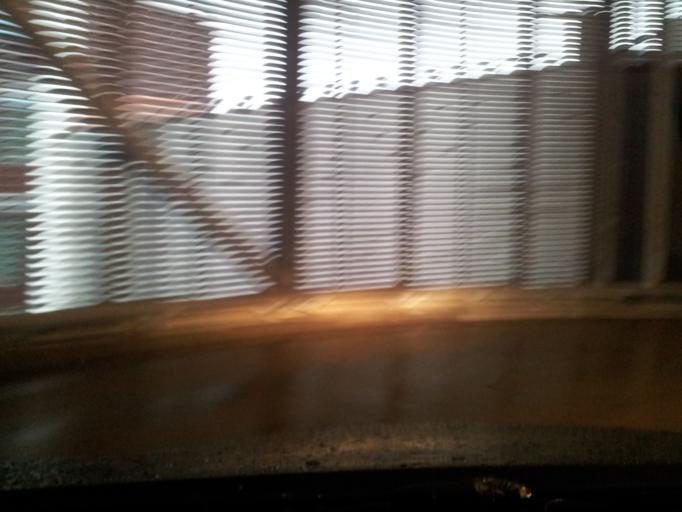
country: FI
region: Uusimaa
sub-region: Helsinki
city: Kilo
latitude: 60.2170
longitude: 24.8131
